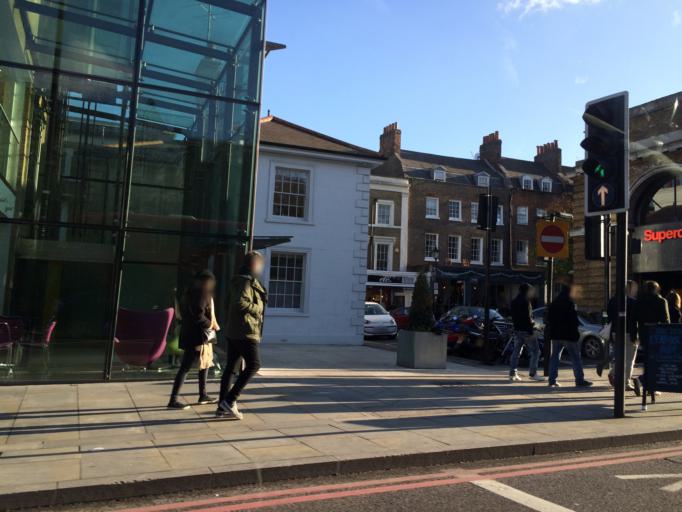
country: GB
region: England
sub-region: Greater London
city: Islington
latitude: 51.5346
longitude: -0.1048
